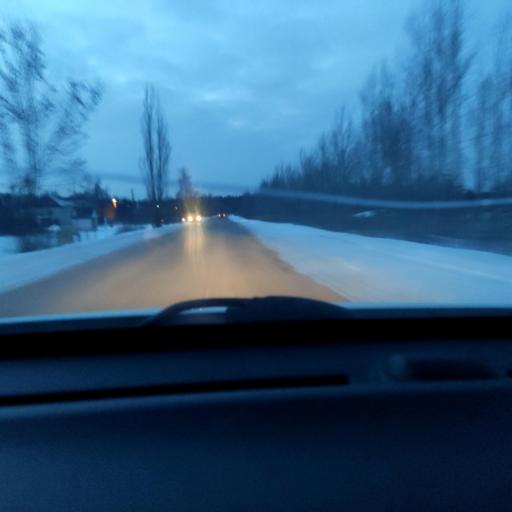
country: RU
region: Voronezj
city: Somovo
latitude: 51.7073
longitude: 39.3702
